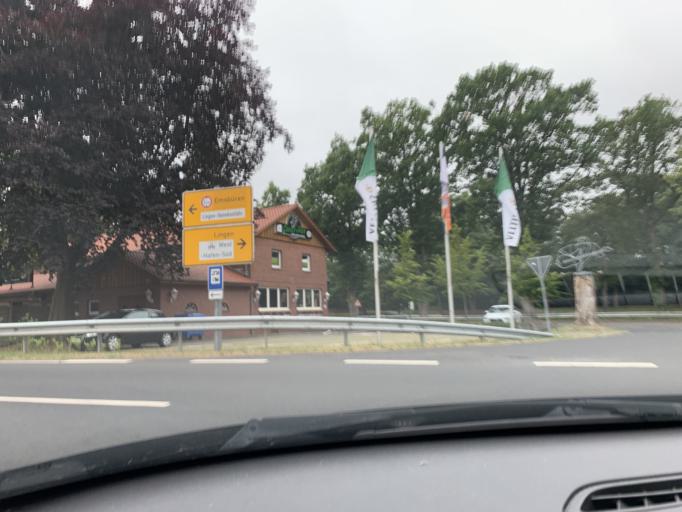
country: DE
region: Lower Saxony
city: Lingen
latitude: 52.4952
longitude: 7.2973
